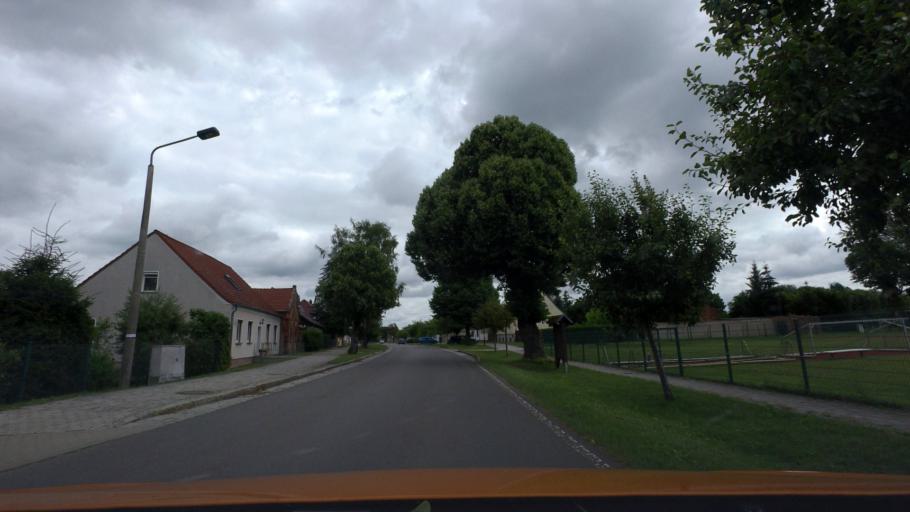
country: DE
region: Brandenburg
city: Neutrebbin
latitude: 52.6679
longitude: 14.2222
